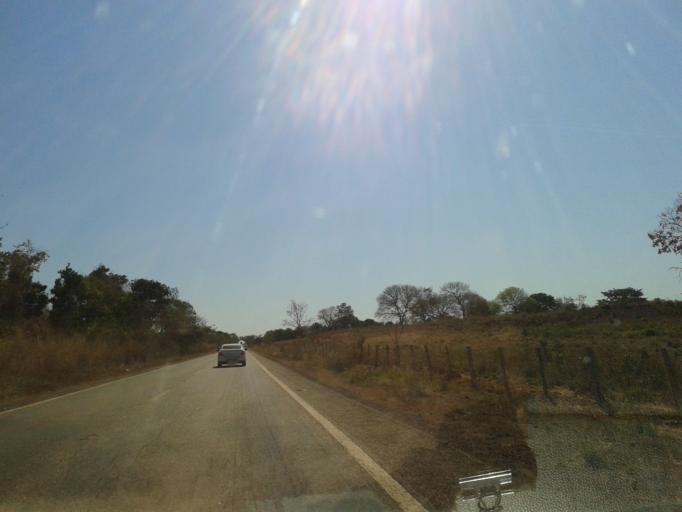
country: BR
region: Goias
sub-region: Crixas
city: Crixas
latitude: -14.1325
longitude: -50.3524
